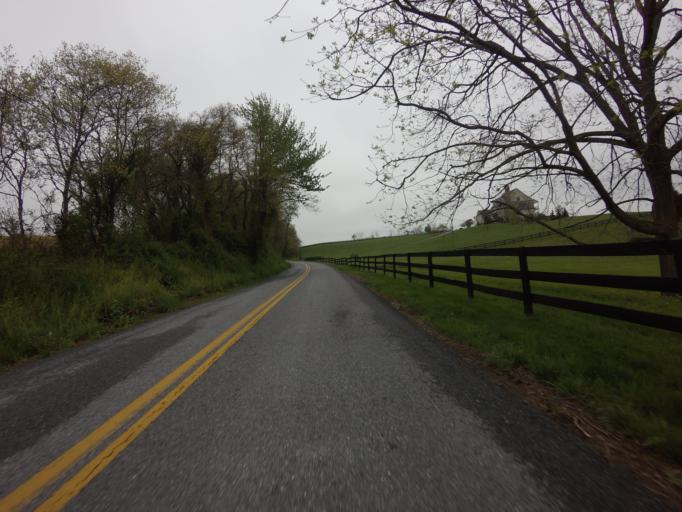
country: US
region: Maryland
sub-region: Carroll County
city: Hampstead
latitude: 39.5707
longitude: -76.7367
